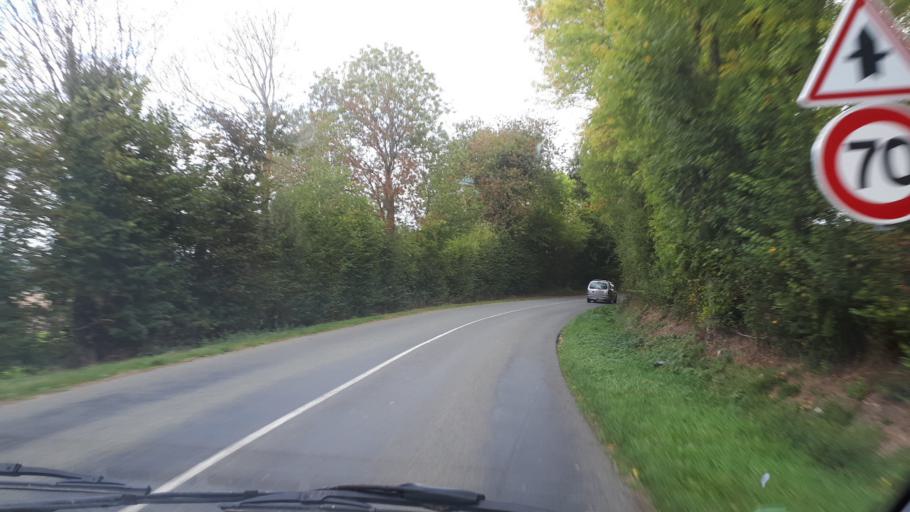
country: FR
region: Centre
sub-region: Departement d'Eure-et-Loir
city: Authon-du-Perche
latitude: 48.2117
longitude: 0.8811
